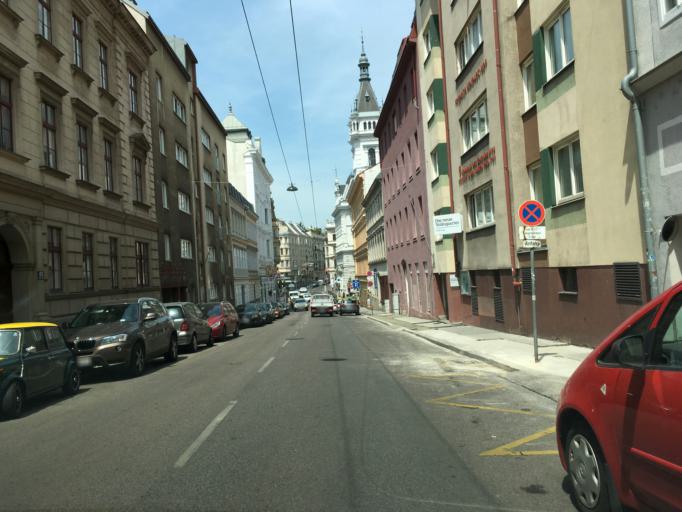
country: AT
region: Vienna
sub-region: Wien Stadt
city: Vienna
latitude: 48.2257
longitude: 16.3422
